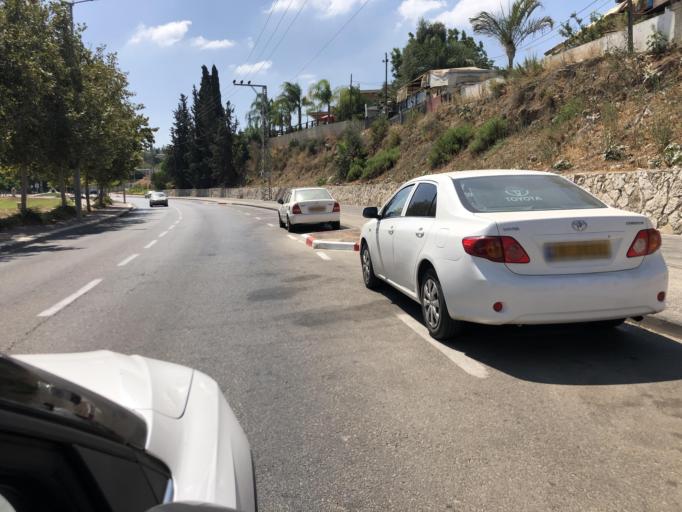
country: IL
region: Central District
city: Rosh Ha'Ayin
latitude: 32.0991
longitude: 34.9573
